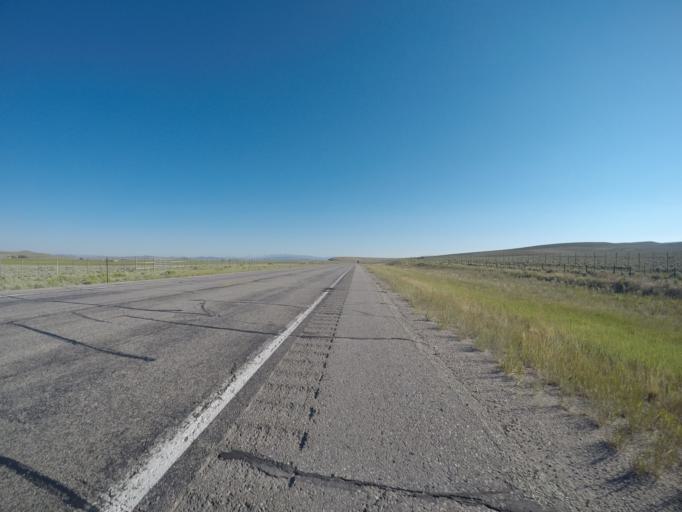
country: US
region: Wyoming
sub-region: Sublette County
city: Pinedale
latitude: 42.9297
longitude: -110.0810
